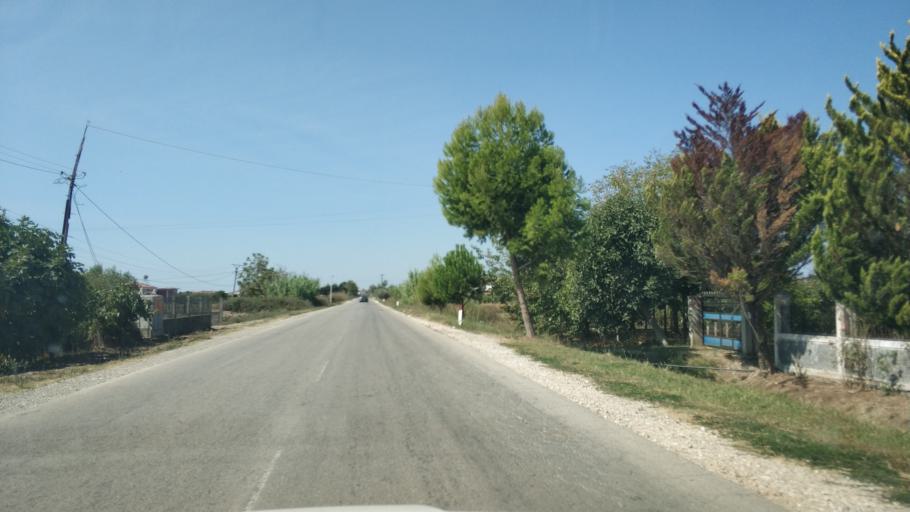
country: AL
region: Fier
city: Terbuf
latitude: 41.0520
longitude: 19.5906
